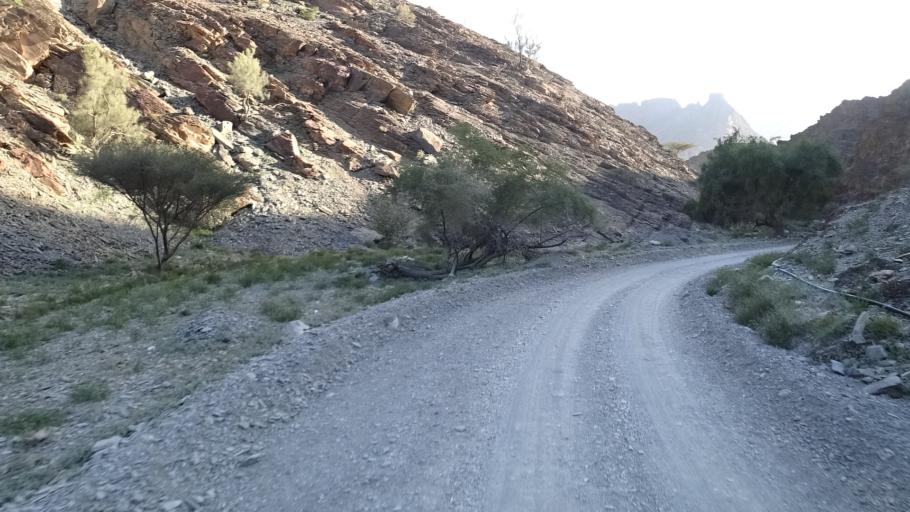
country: OM
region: Al Batinah
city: Rustaq
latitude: 23.2641
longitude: 57.3970
